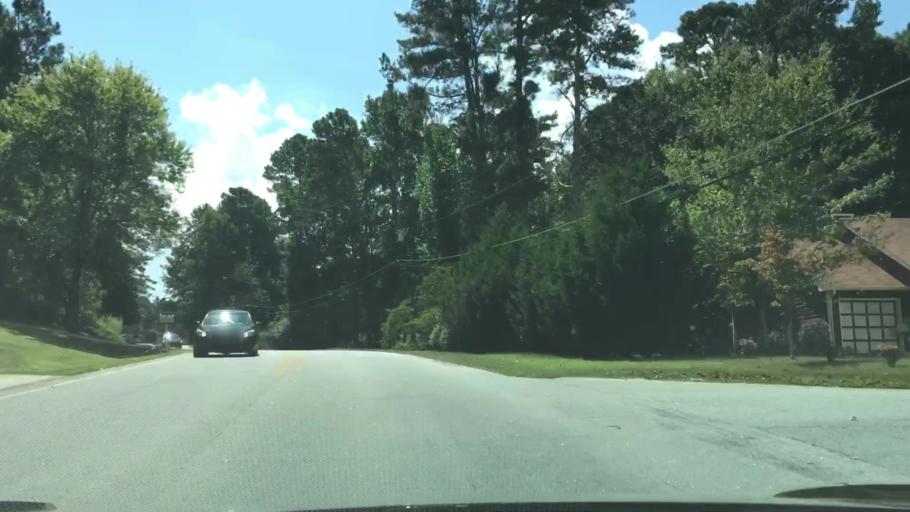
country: US
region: Georgia
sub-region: Gwinnett County
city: Snellville
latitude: 33.8636
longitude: -84.0502
